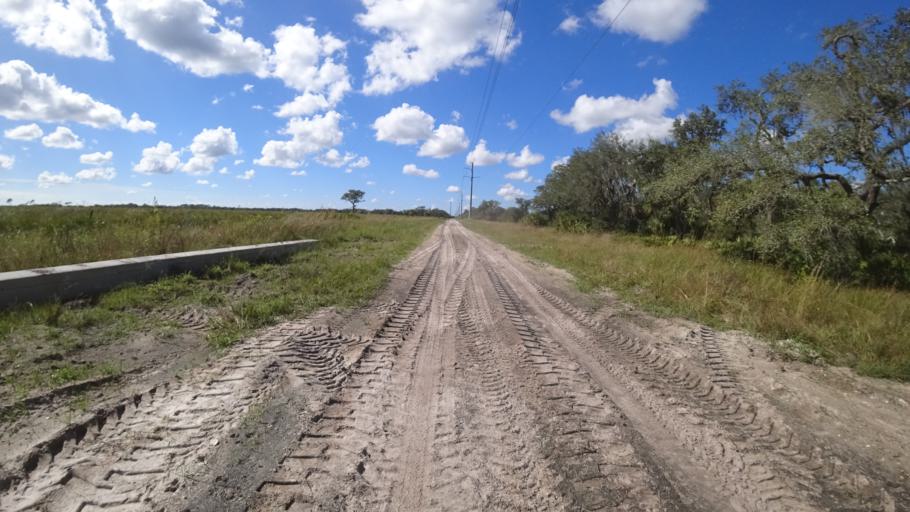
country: US
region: Florida
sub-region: Sarasota County
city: Lake Sarasota
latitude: 27.2440
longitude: -82.2691
